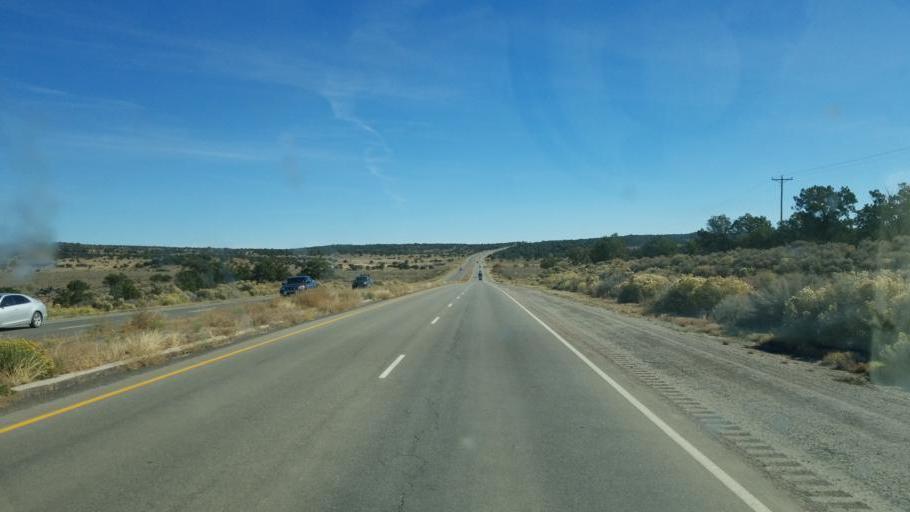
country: US
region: New Mexico
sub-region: McKinley County
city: Twin Lakes
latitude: 35.6329
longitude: -108.8991
